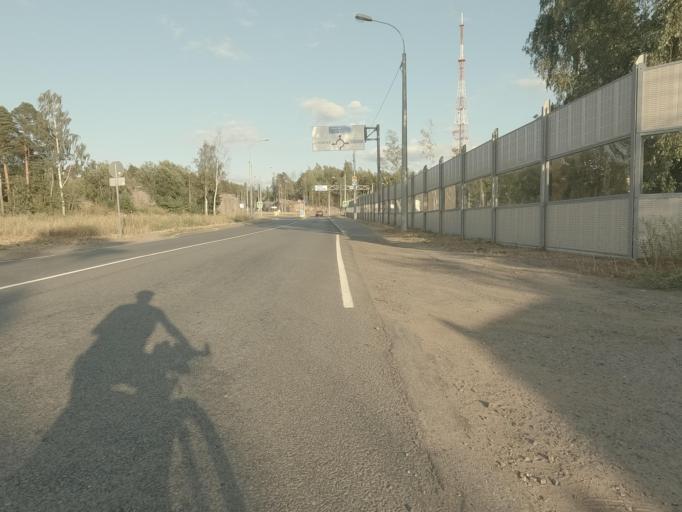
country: RU
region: Leningrad
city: Vyborg
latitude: 60.7244
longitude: 28.7657
